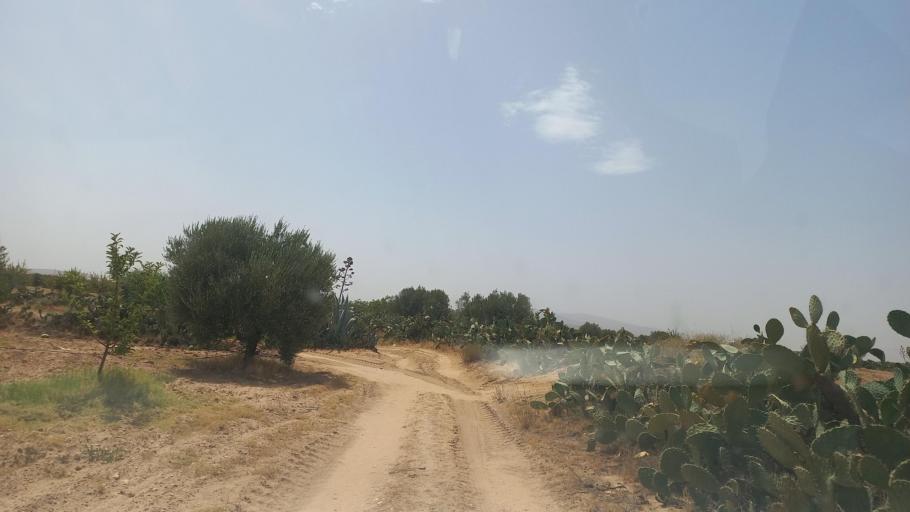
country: TN
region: Al Qasrayn
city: Kasserine
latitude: 35.2601
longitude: 9.0052
